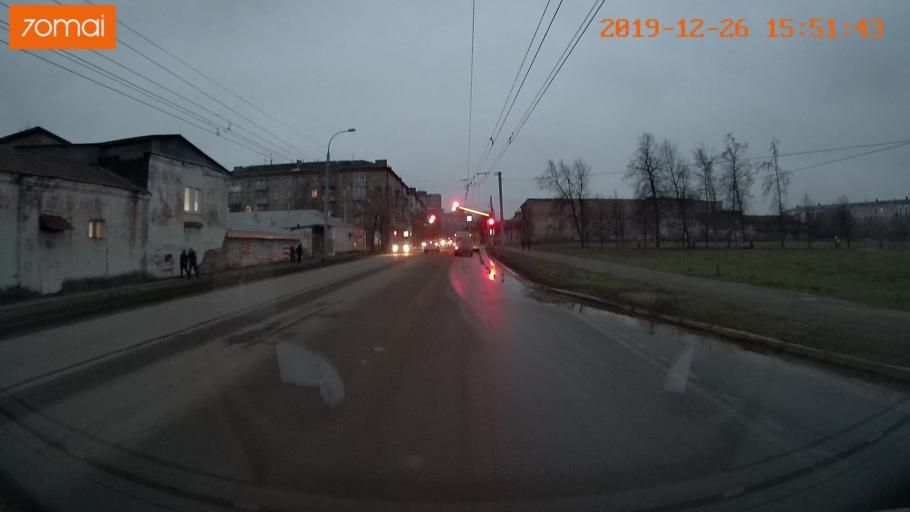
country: RU
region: Jaroslavl
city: Rybinsk
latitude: 58.0520
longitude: 38.8252
